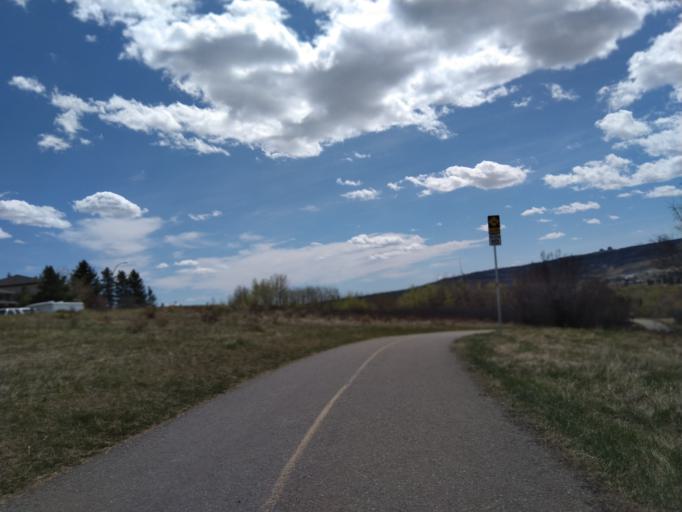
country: CA
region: Alberta
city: Calgary
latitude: 51.0996
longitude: -114.1903
